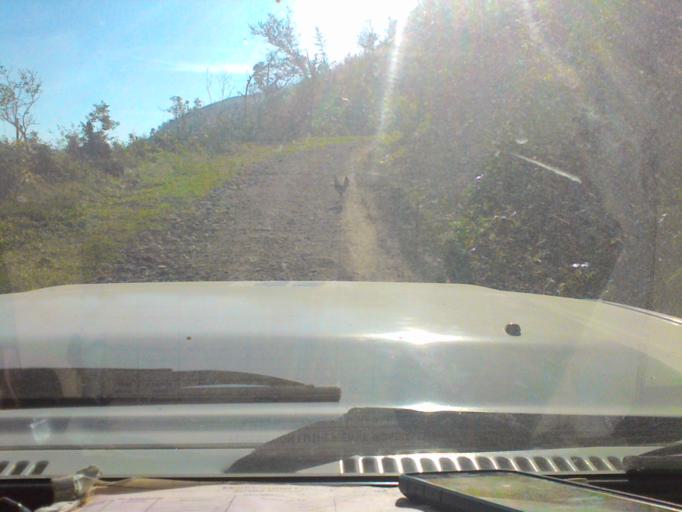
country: HT
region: Grandans
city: Jeremie
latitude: 18.5165
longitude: -74.0835
